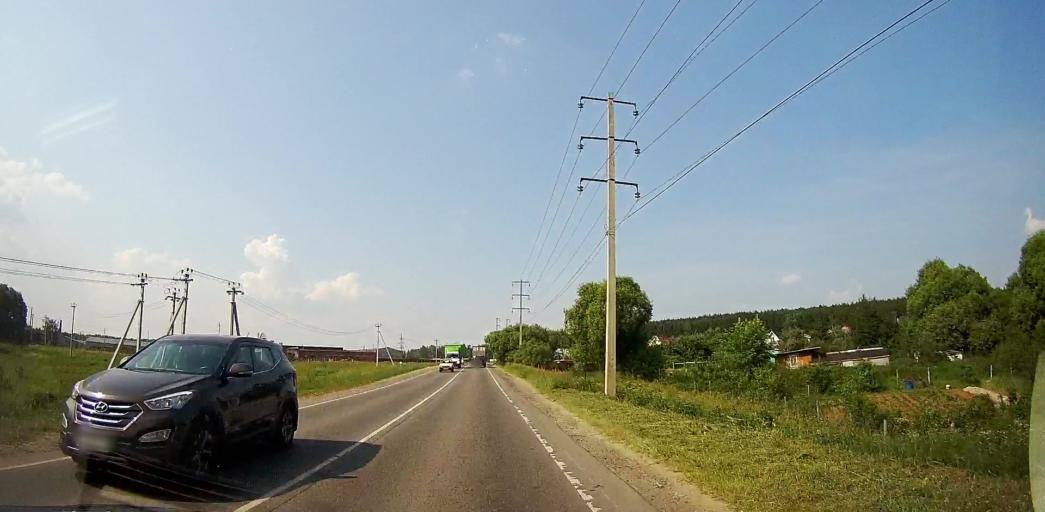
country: RU
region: Moskovskaya
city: Barybino
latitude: 55.2756
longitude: 37.9163
